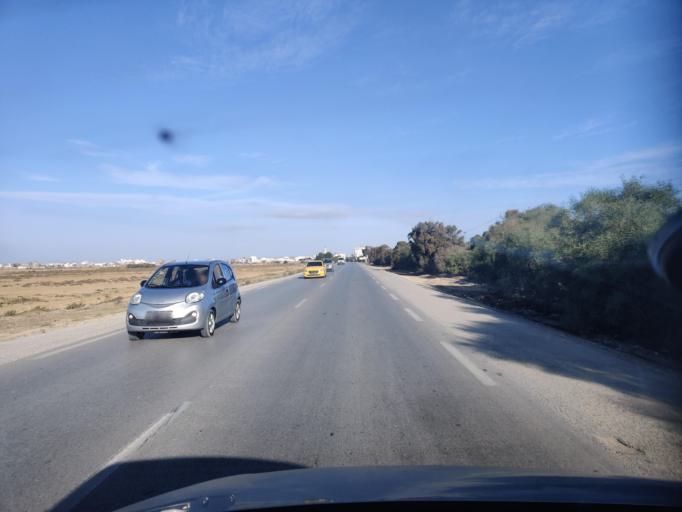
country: TN
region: Ariana
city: Ariana
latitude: 36.9505
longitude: 10.2370
